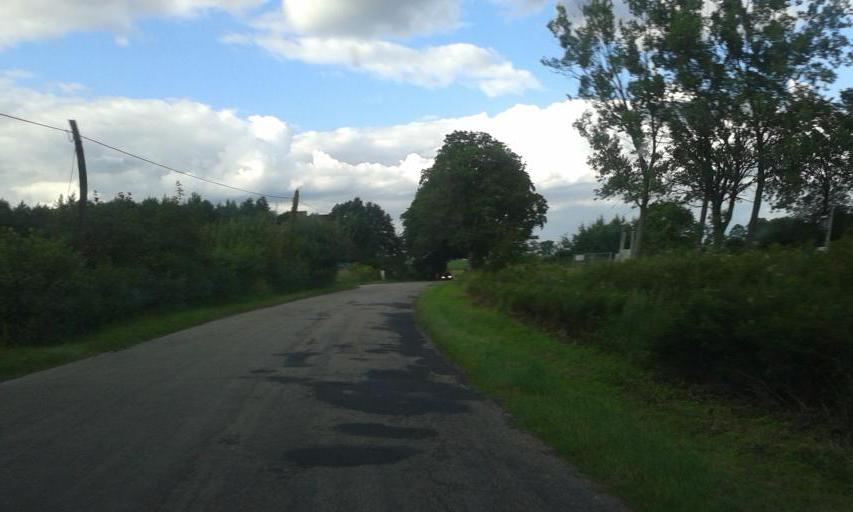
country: PL
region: West Pomeranian Voivodeship
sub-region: Powiat szczecinecki
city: Barwice
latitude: 53.6833
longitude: 16.3415
